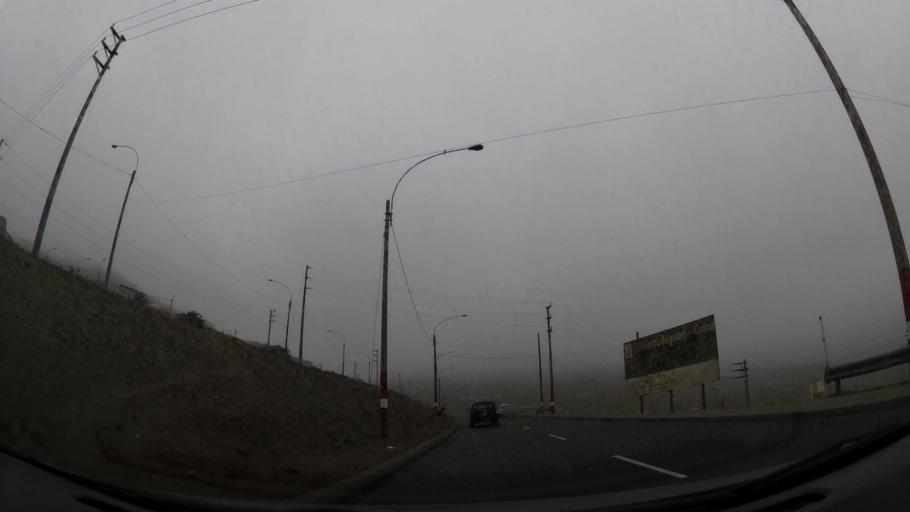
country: PE
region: Lima
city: Ventanilla
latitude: -11.8497
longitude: -77.1229
